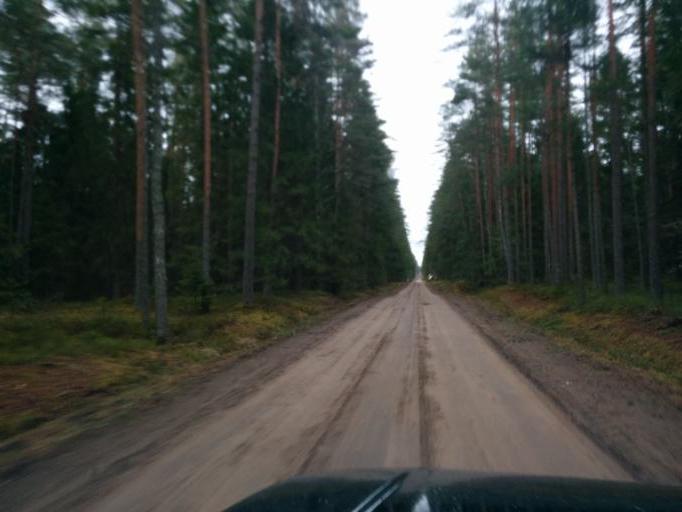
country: LV
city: Tireli
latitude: 56.7915
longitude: 23.6532
